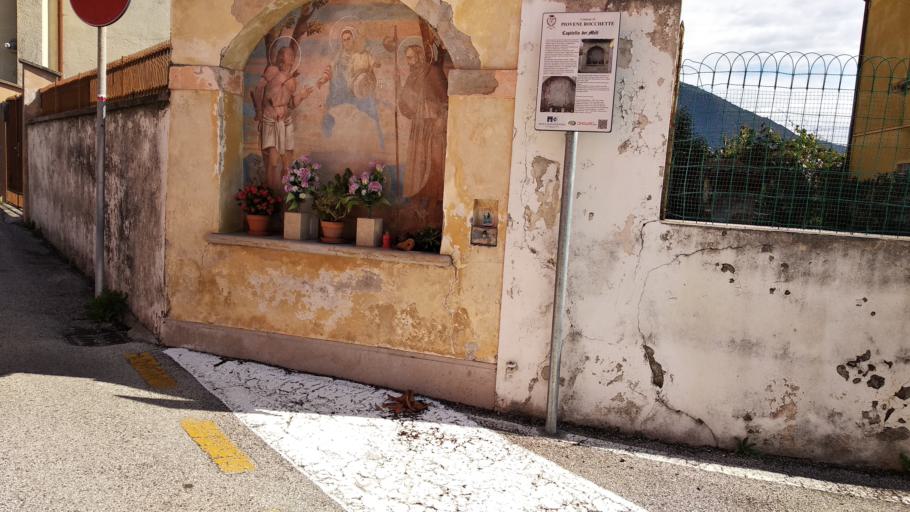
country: IT
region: Veneto
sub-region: Provincia di Vicenza
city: Piovene Rocchette
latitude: 45.7560
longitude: 11.4304
